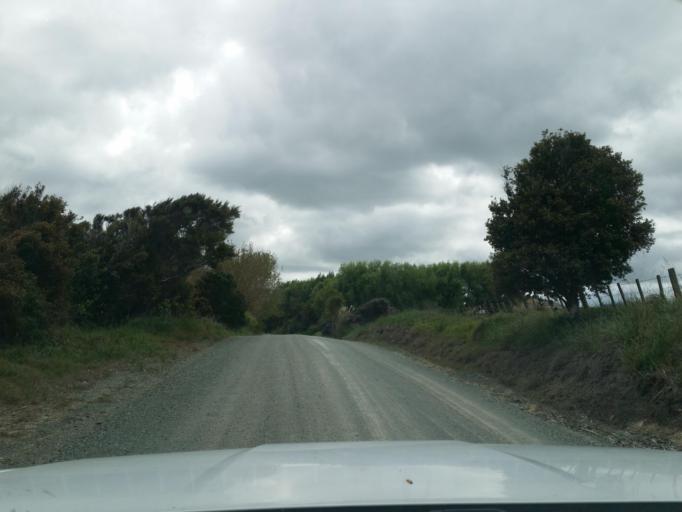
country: NZ
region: Auckland
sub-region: Auckland
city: Wellsford
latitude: -36.2605
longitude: 174.3695
